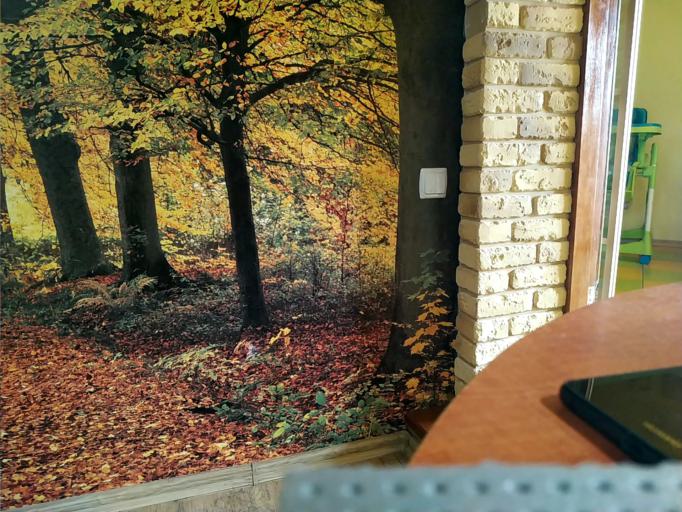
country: RU
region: Tverskaya
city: Kalashnikovo
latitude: 57.3080
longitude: 35.1107
